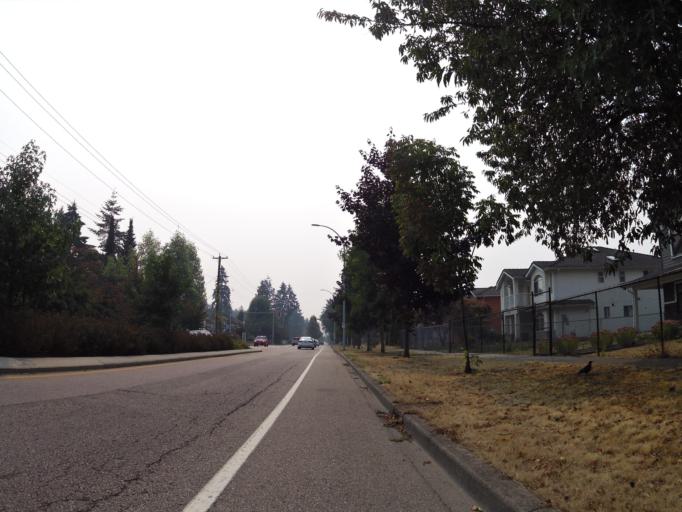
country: CA
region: British Columbia
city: Surrey
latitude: 49.1322
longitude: -122.8567
